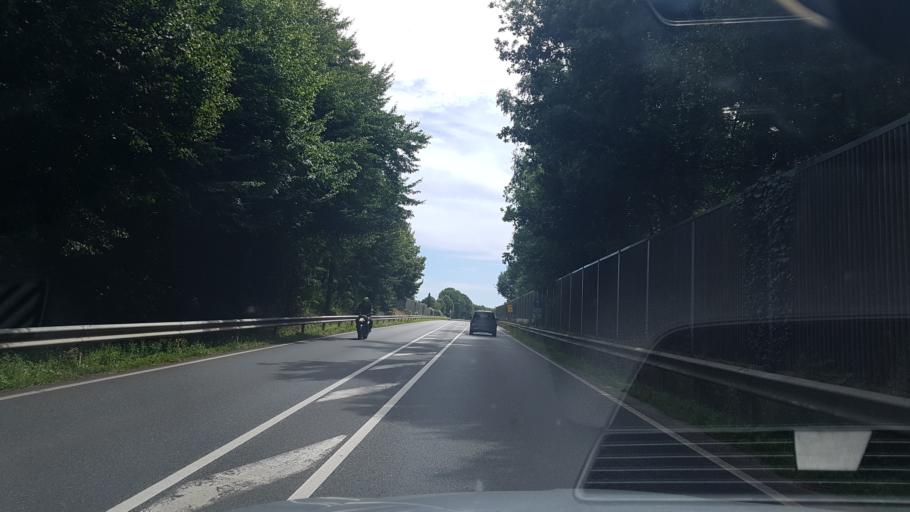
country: DE
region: Schleswig-Holstein
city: Brugge
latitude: 54.1770
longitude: 10.0594
